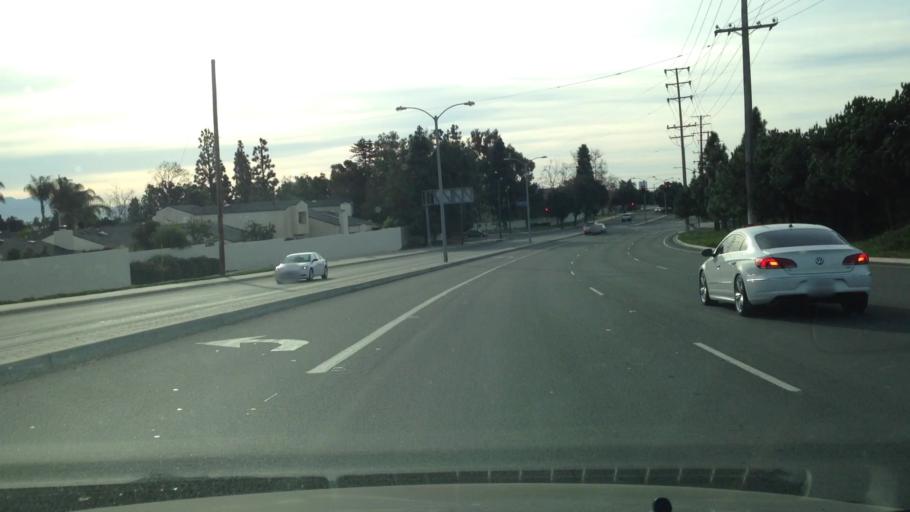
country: US
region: California
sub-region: Ventura County
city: Saticoy
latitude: 34.2726
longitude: -119.1896
